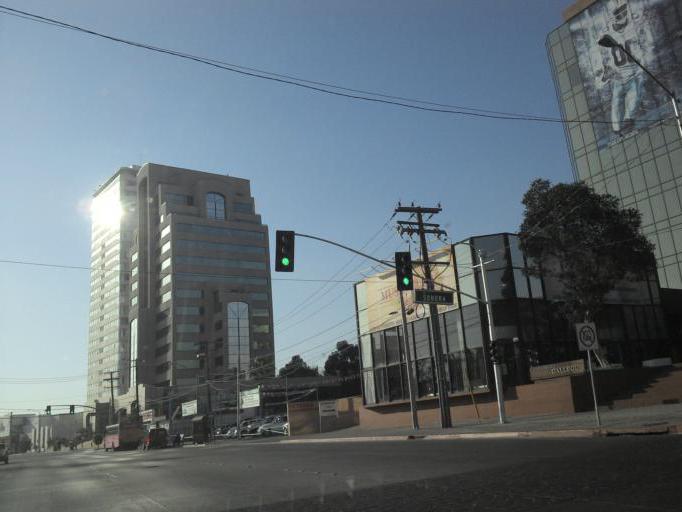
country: MX
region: Baja California
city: Tijuana
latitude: 32.5145
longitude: -117.0111
